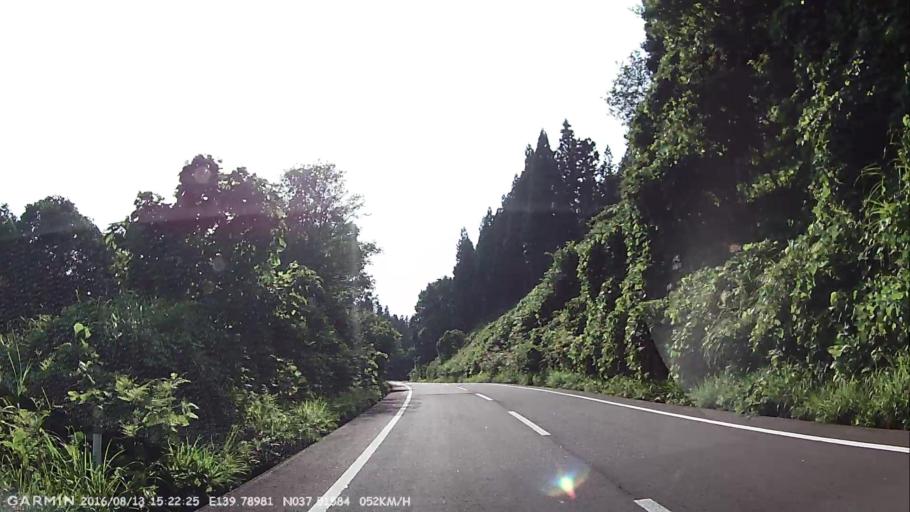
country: JP
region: Fukushima
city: Kitakata
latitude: 37.5159
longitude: 139.7898
